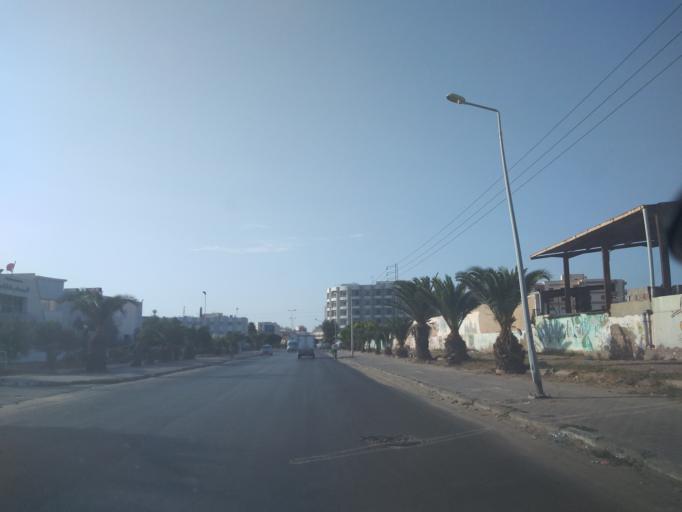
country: TN
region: Safaqis
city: Sfax
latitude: 34.7276
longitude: 10.7548
